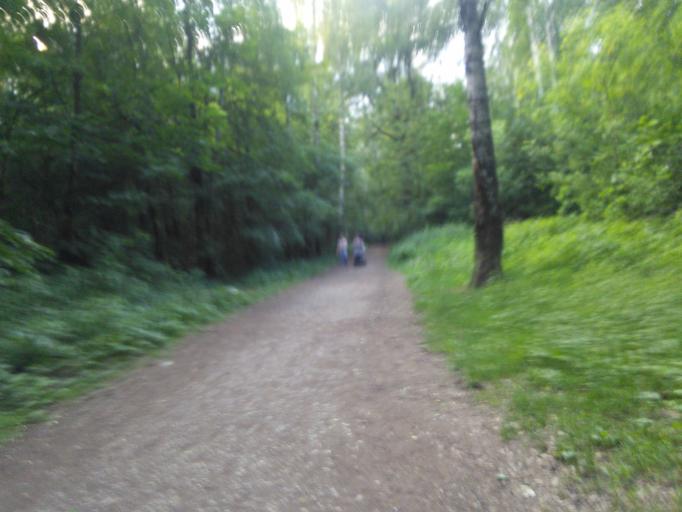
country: RU
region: Moscow
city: Sokol'niki
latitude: 55.8125
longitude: 37.6677
